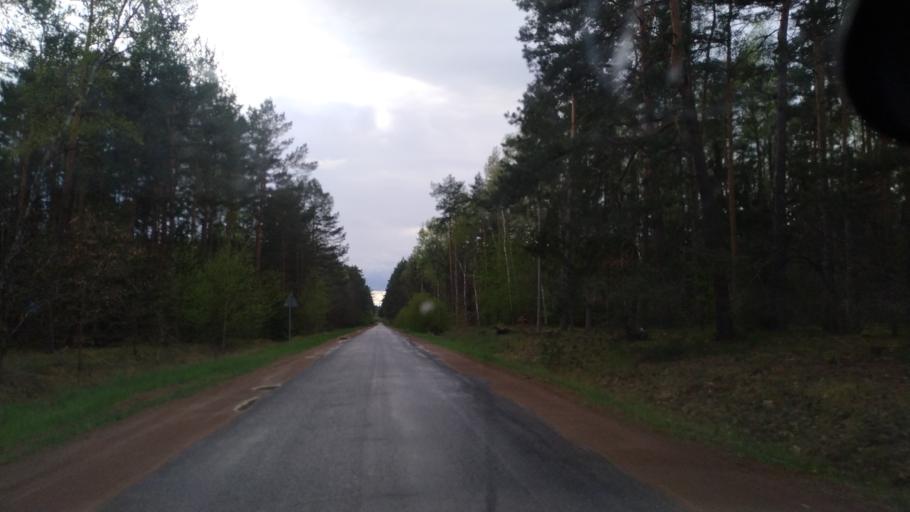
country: PL
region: Pomeranian Voivodeship
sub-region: Powiat starogardzki
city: Osiek
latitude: 53.6944
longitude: 18.5494
